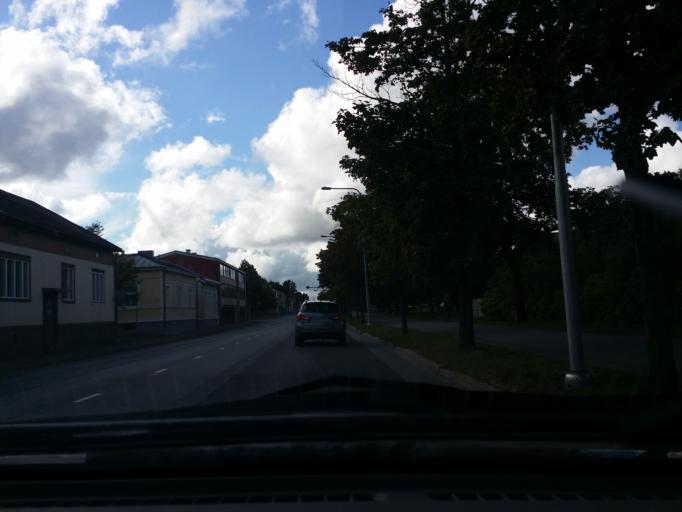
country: FI
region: Satakunta
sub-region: Pori
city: Pori
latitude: 61.4850
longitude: 21.7731
